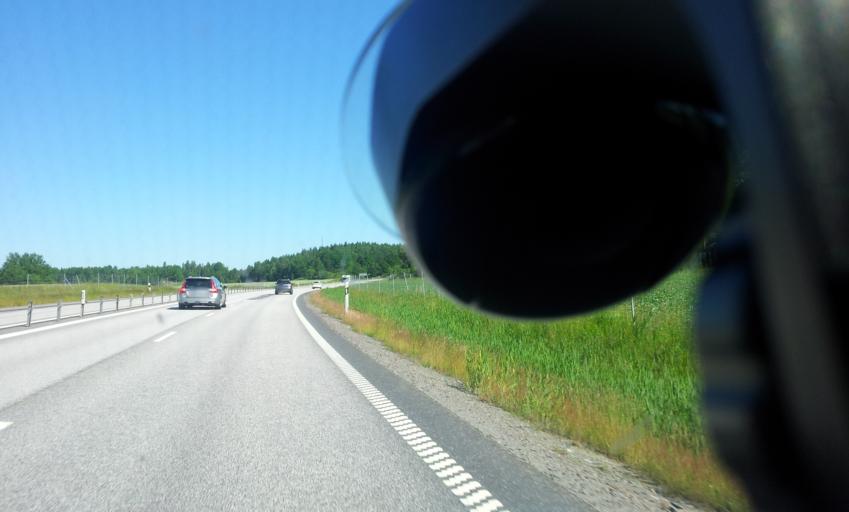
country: SE
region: OEstergoetland
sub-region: Soderkopings Kommun
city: Soederkoeping
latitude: 58.3863
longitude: 16.4120
